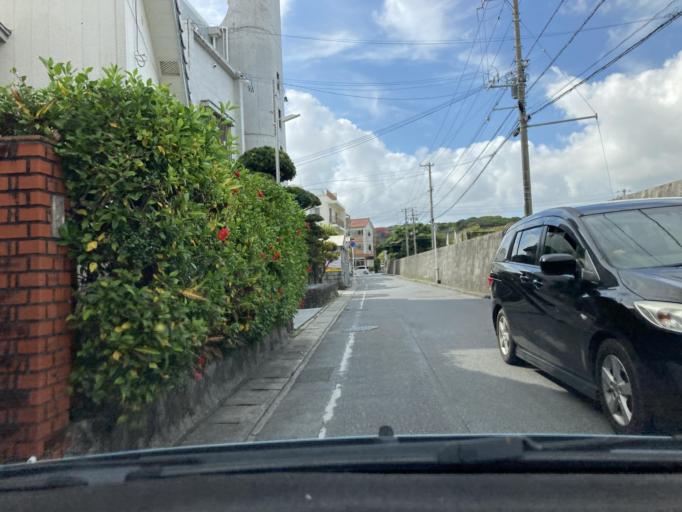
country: JP
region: Okinawa
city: Naha-shi
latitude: 26.2213
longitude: 127.7181
